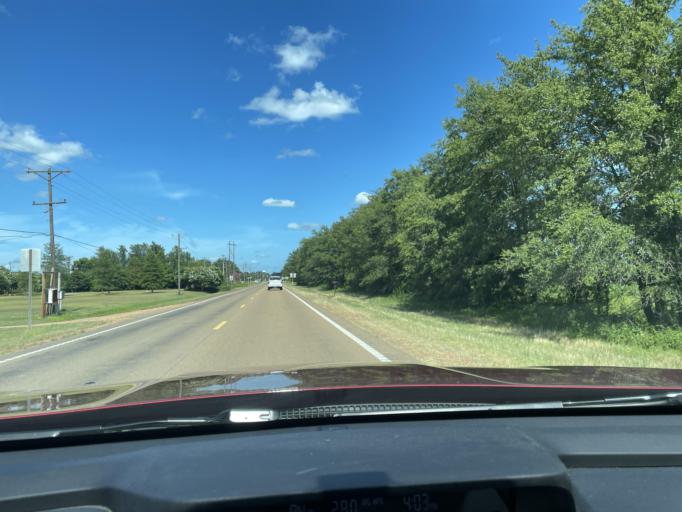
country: US
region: Mississippi
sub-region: Humphreys County
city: Belzoni
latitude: 33.1838
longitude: -90.5033
